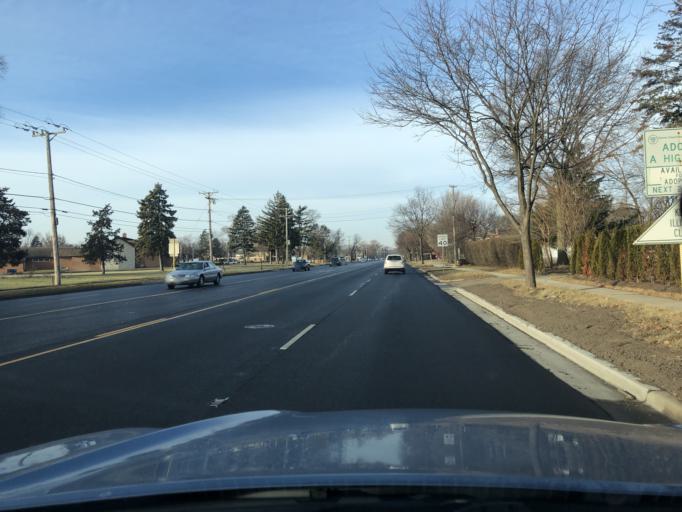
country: US
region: Illinois
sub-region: Cook County
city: Mount Prospect
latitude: 42.0476
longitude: -87.9423
